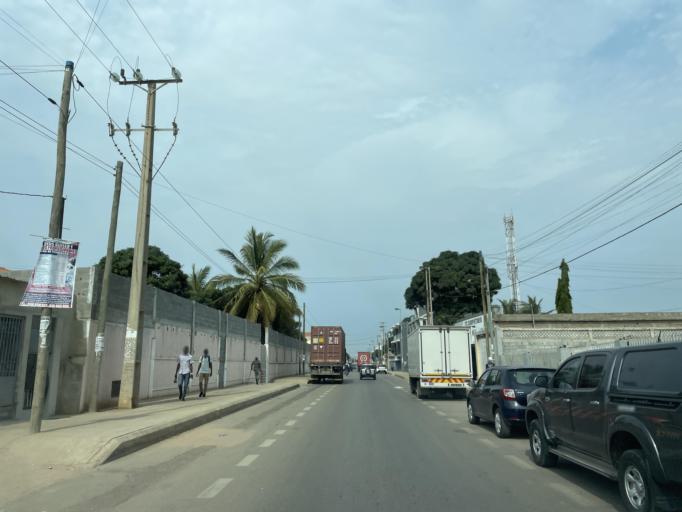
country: AO
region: Luanda
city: Luanda
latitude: -8.8974
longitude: 13.1889
